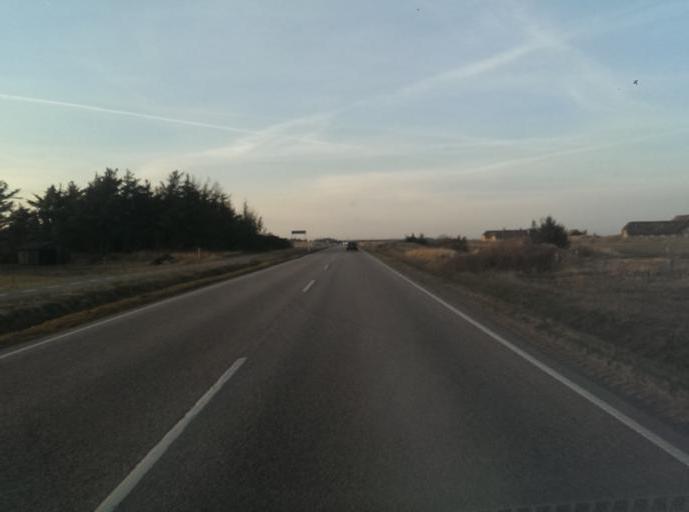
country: DK
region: Central Jutland
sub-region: Ringkobing-Skjern Kommune
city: Hvide Sande
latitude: 56.0691
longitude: 8.1216
